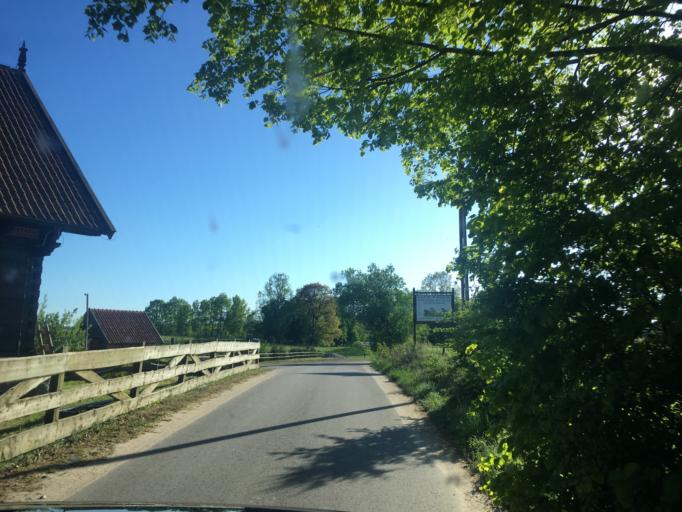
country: PL
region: Warmian-Masurian Voivodeship
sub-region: Powiat piski
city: Ruciane-Nida
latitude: 53.6887
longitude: 21.4758
